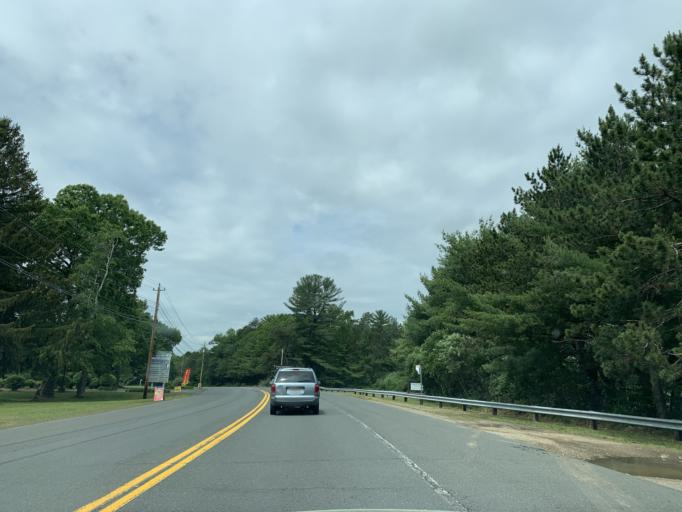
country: US
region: Massachusetts
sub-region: Hampshire County
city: Southampton
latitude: 42.1784
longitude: -72.6902
